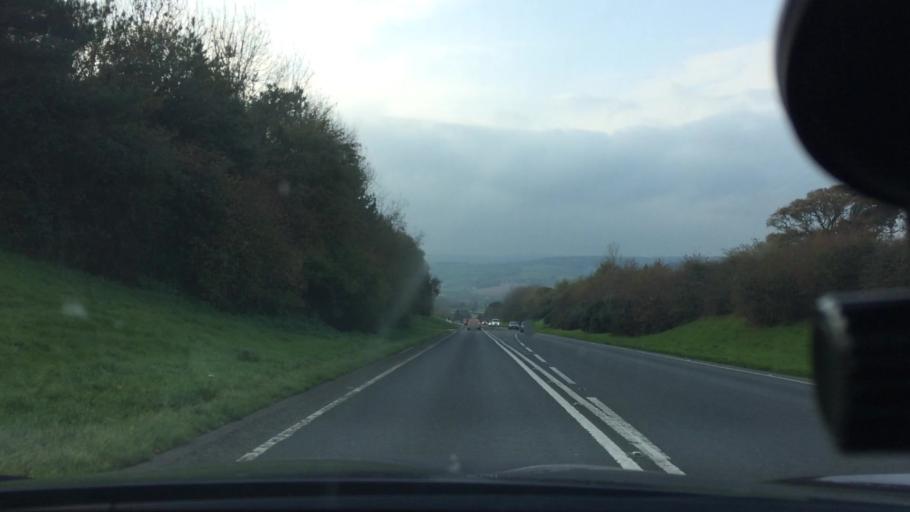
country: GB
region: England
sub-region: Devon
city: Axminster
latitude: 50.7673
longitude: -2.9855
